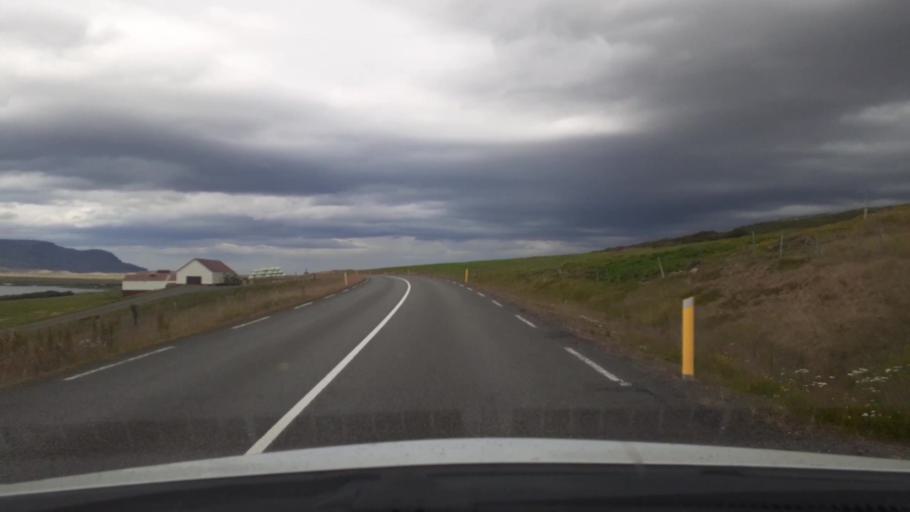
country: IS
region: West
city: Borgarnes
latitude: 64.5435
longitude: -21.5768
